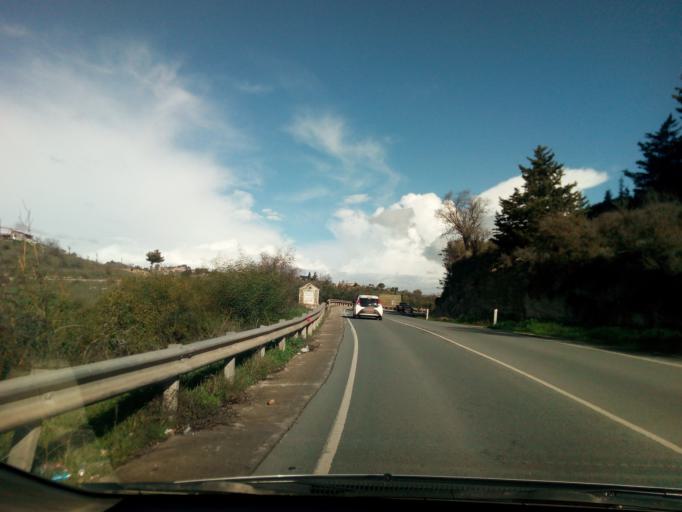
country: CY
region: Pafos
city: Tala
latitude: 34.8741
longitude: 32.4811
